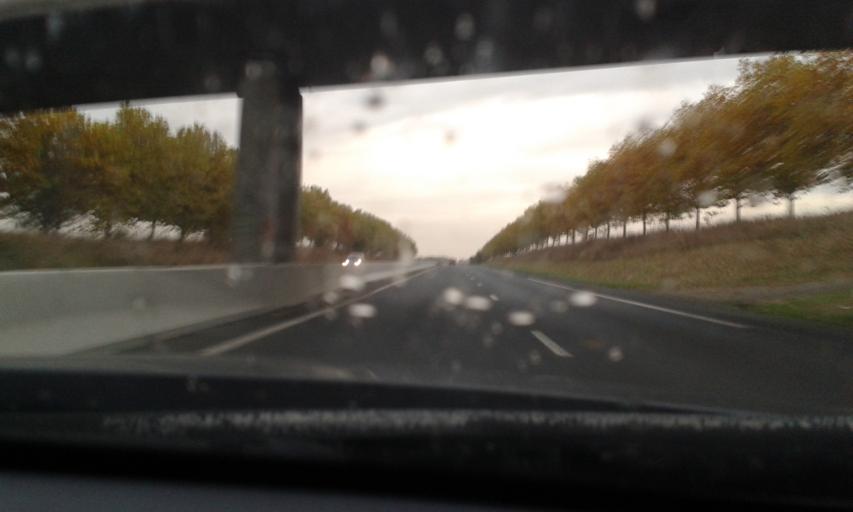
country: FR
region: Haute-Normandie
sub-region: Departement de la Seine-Maritime
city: Saint-Martin-Osmonville
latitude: 49.6286
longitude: 1.2636
